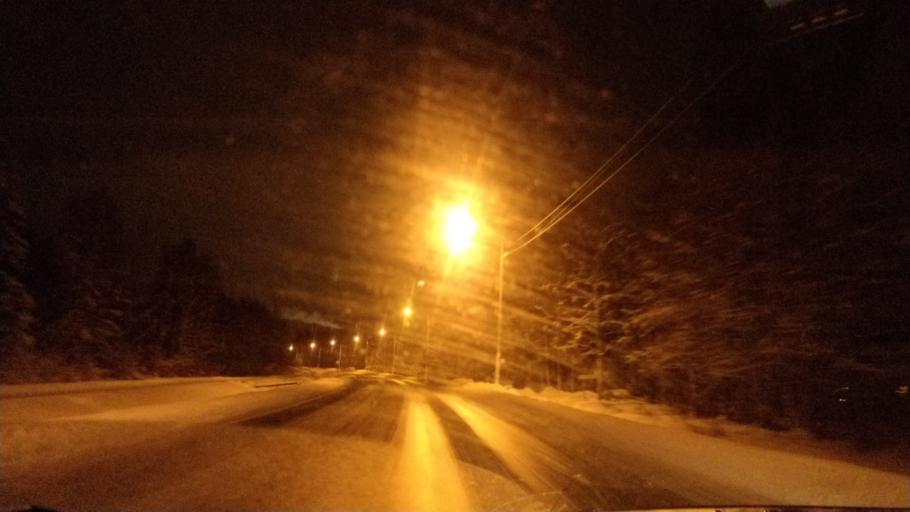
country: FI
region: Lapland
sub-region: Rovaniemi
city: Rovaniemi
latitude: 66.3868
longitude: 25.3769
